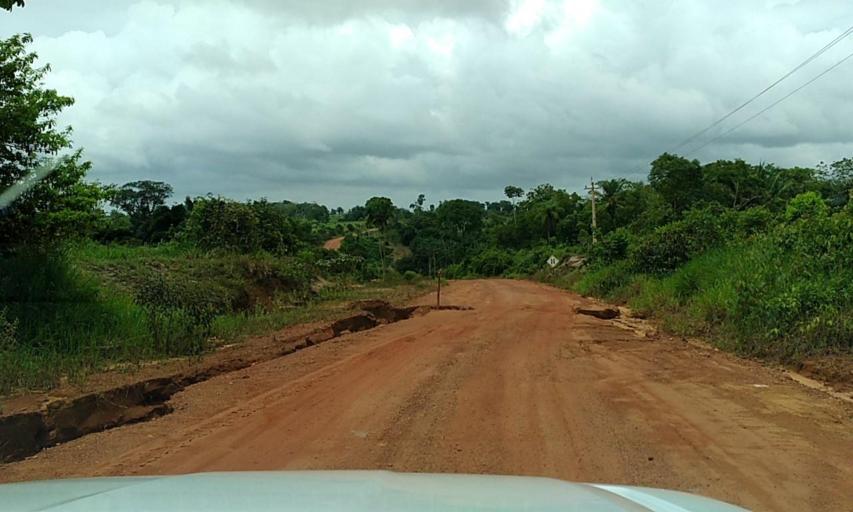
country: BR
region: Para
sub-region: Senador Jose Porfirio
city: Senador Jose Porfirio
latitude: -2.6172
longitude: -51.8685
